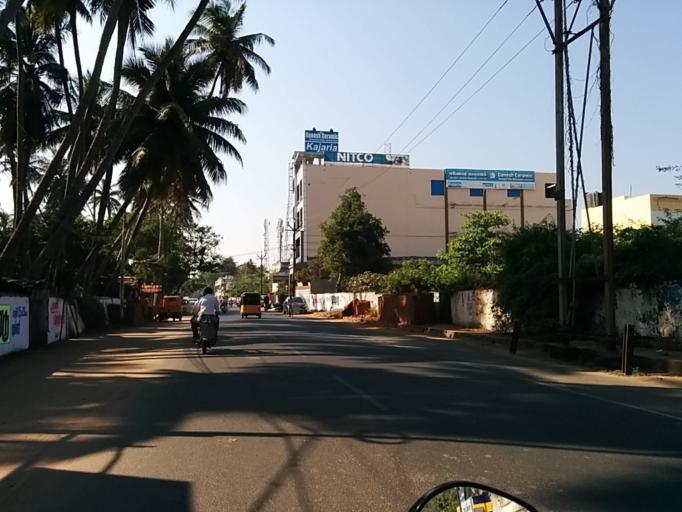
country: IN
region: Pondicherry
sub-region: Puducherry
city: Puducherry
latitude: 11.9538
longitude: 79.8288
